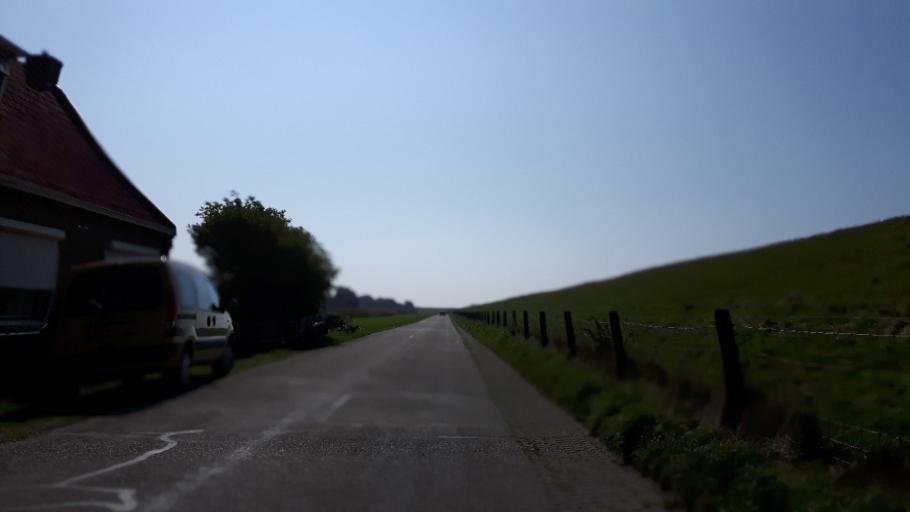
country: NL
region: Friesland
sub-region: Sudwest Fryslan
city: Makkum
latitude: 53.0883
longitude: 5.3816
